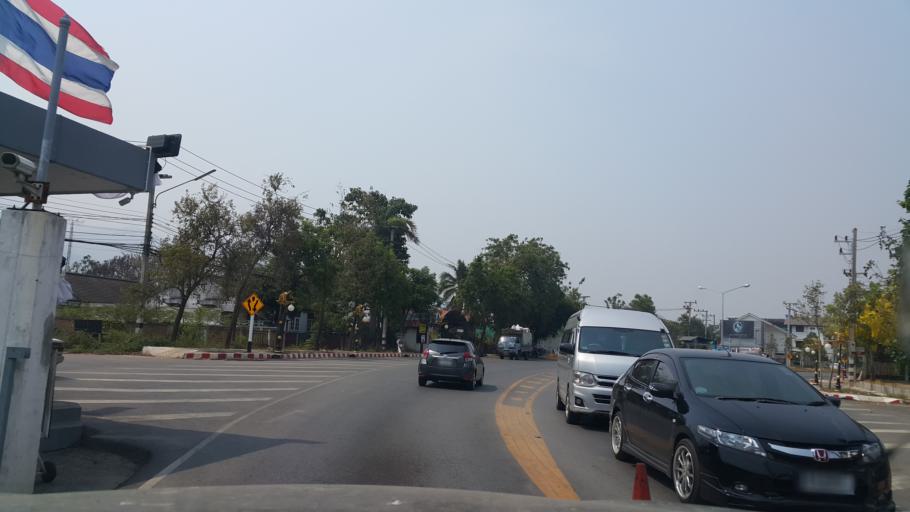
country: TH
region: Chiang Mai
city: Chiang Mai
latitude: 18.7868
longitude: 98.9628
